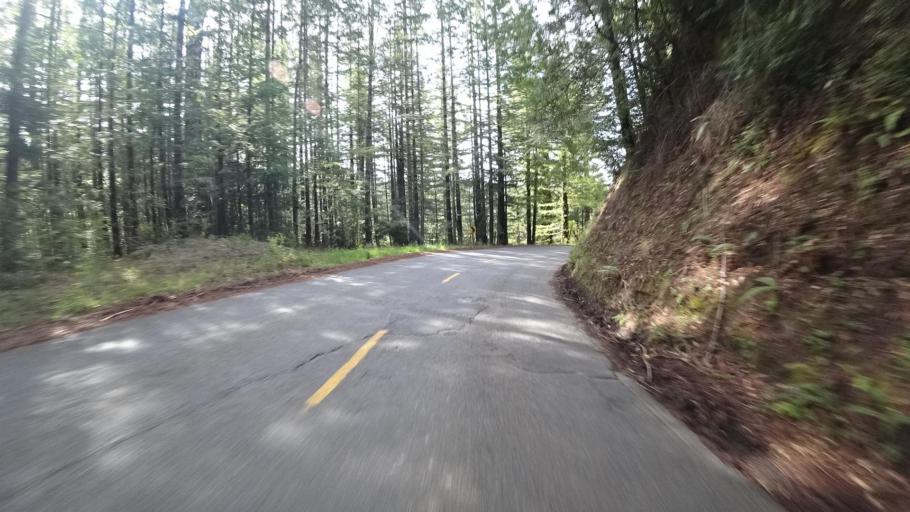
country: US
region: California
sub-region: Humboldt County
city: Bayside
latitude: 40.7575
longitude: -124.0190
